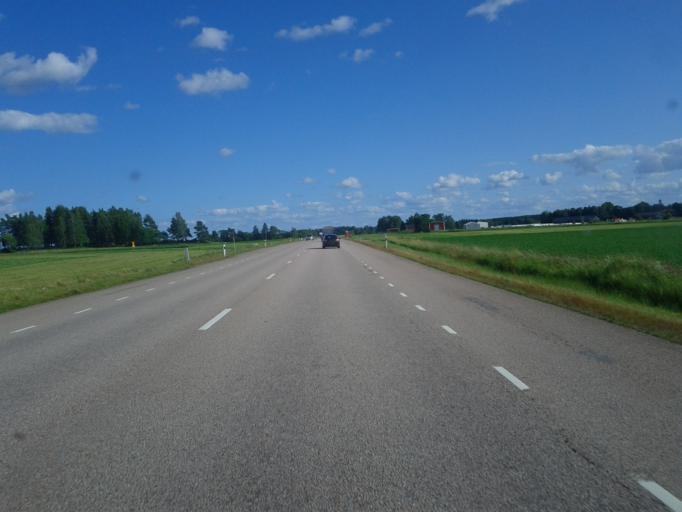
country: SE
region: Uppsala
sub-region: Enkopings Kommun
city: Enkoping
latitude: 59.6907
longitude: 17.0310
